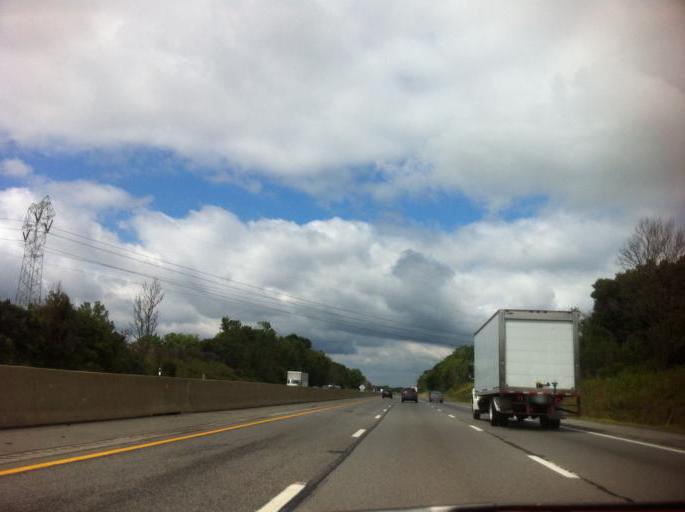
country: US
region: Ohio
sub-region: Portage County
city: Streetsboro
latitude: 41.2516
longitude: -81.3285
